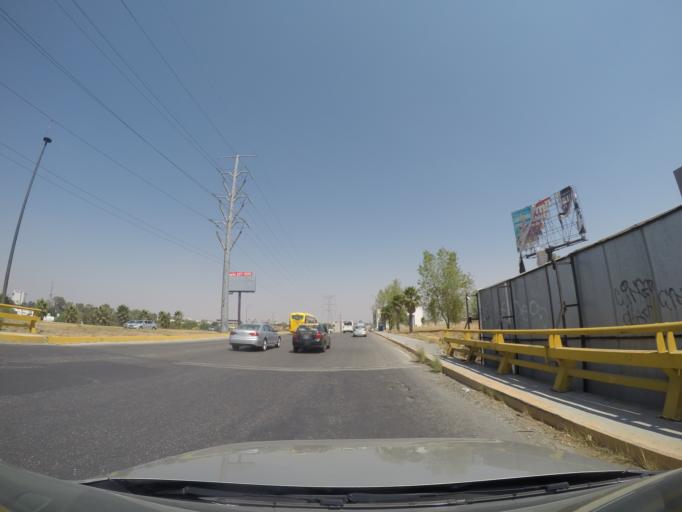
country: MX
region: Puebla
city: Tlazcalancingo
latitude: 19.0190
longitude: -98.2489
